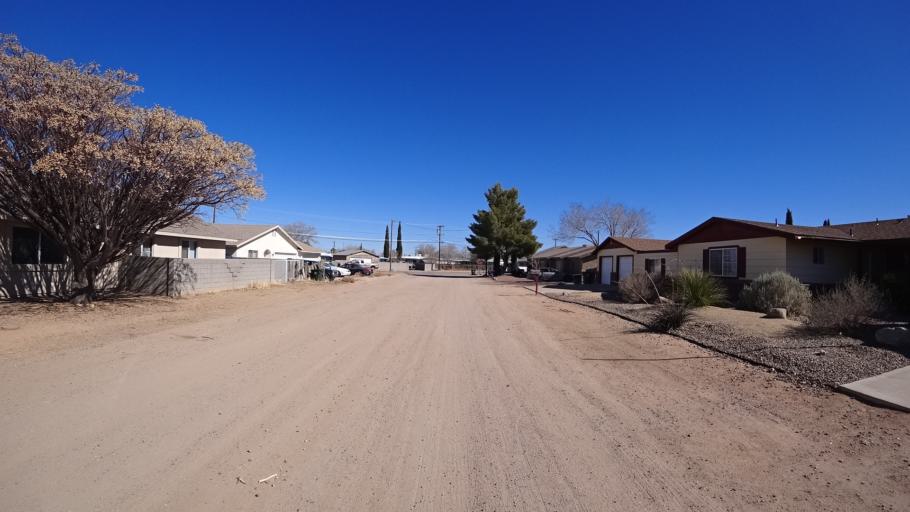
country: US
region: Arizona
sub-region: Mohave County
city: Kingman
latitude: 35.2099
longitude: -114.0223
